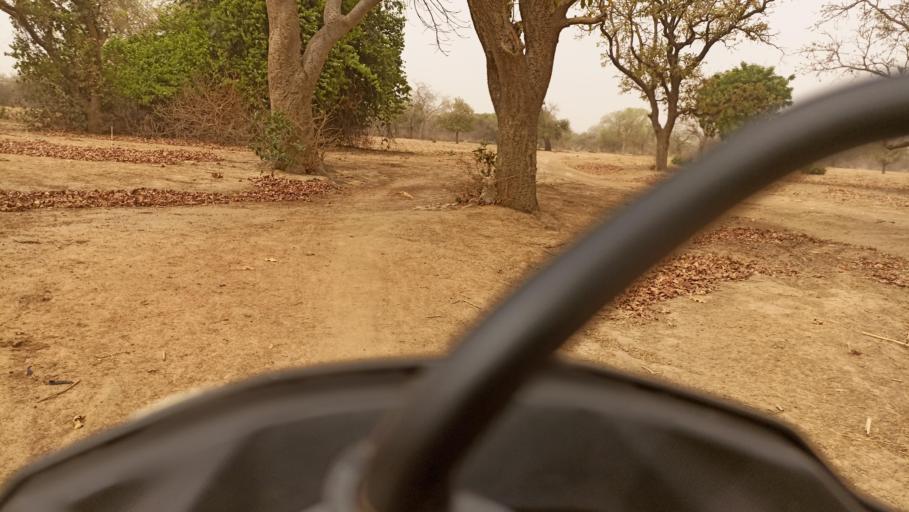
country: BF
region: Nord
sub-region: Province du Zondoma
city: Gourcy
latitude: 13.2501
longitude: -2.6042
